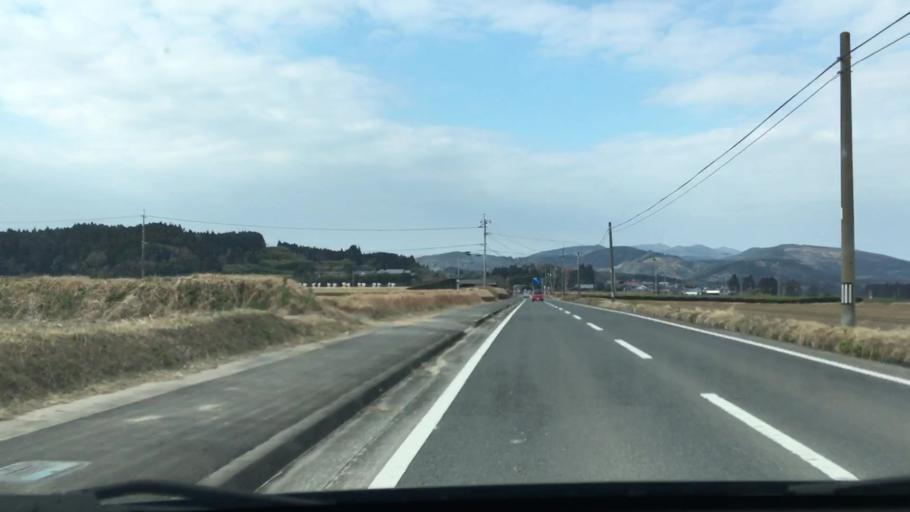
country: JP
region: Miyazaki
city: Kushima
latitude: 31.5161
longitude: 131.2393
